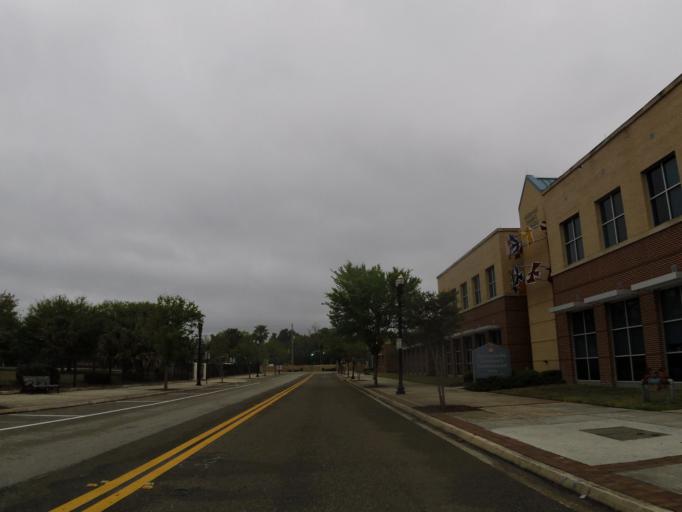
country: US
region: Florida
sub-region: Duval County
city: Jacksonville
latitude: 30.3353
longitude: -81.6426
